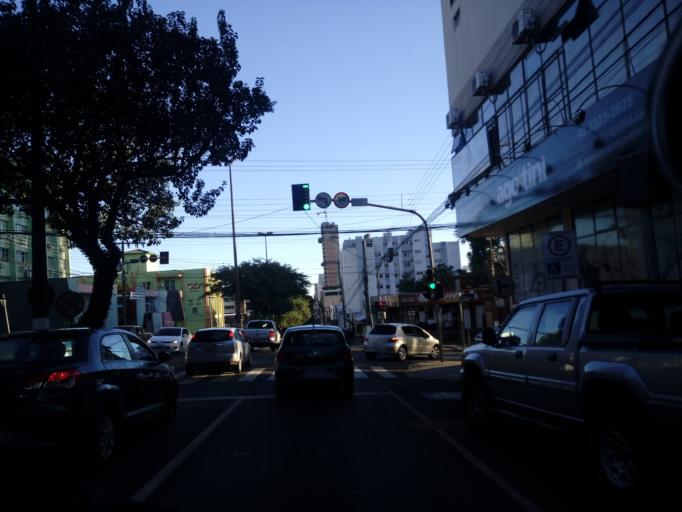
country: BR
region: Santa Catarina
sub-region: Chapeco
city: Chapeco
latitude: -27.1046
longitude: -52.6122
